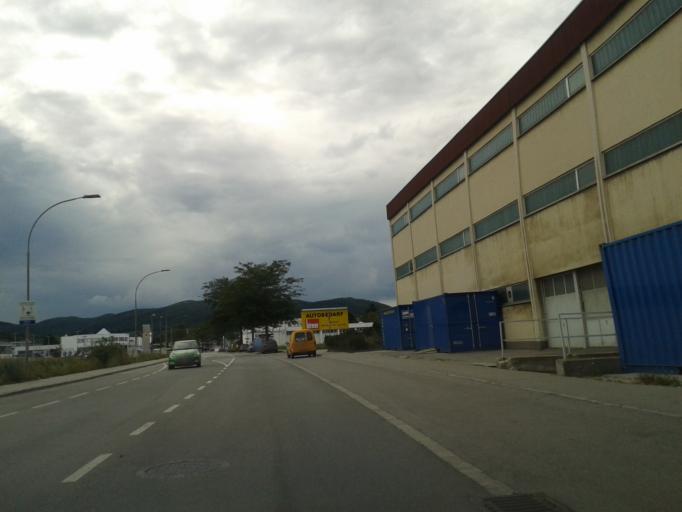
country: AT
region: Lower Austria
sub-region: Politischer Bezirk Modling
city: Brunn am Gebirge
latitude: 48.1238
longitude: 16.2921
